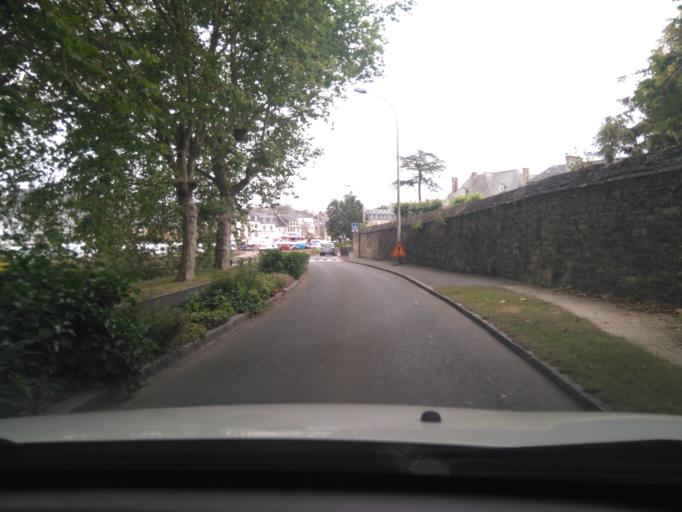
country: FR
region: Brittany
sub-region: Departement des Cotes-d'Armor
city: Lannion
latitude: 48.7311
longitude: -3.4631
